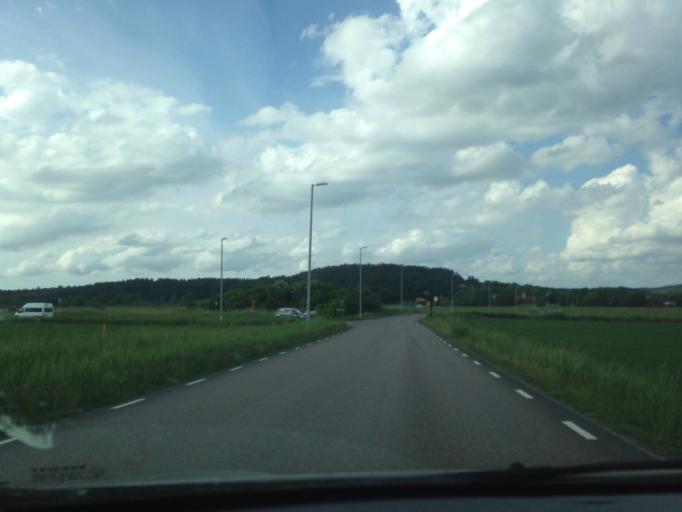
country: SE
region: Vaestra Goetaland
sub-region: Goteborg
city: Goeteborg
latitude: 57.7701
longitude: 11.9309
